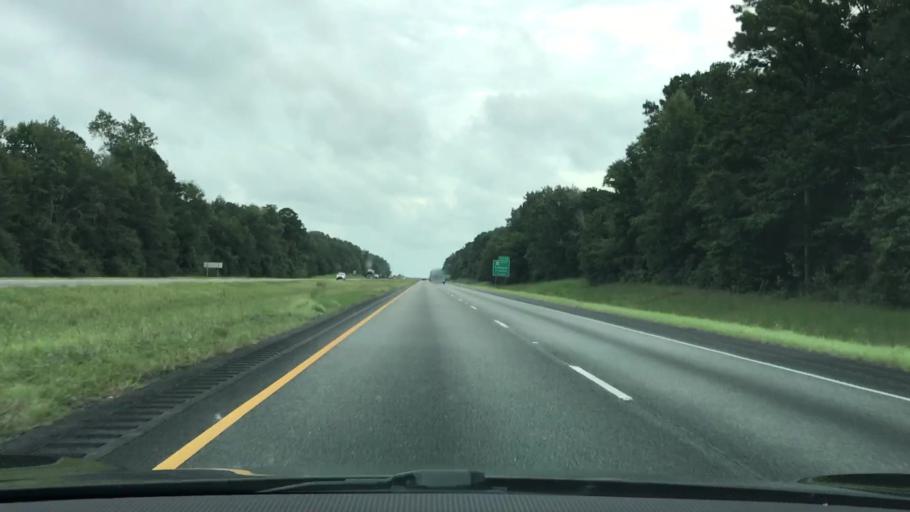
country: US
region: Alabama
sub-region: Macon County
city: Tuskegee
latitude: 32.4449
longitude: -85.8110
